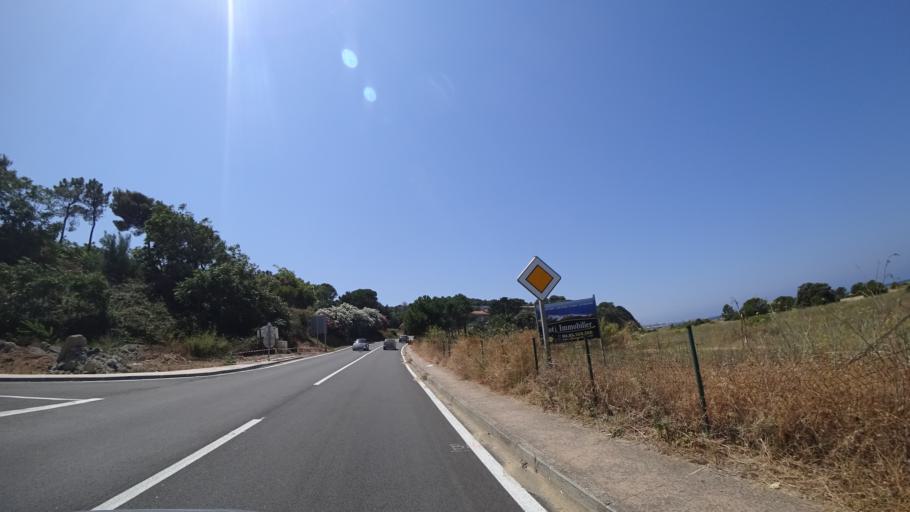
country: FR
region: Corsica
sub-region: Departement de la Corse-du-Sud
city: Propriano
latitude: 41.6834
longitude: 8.9207
